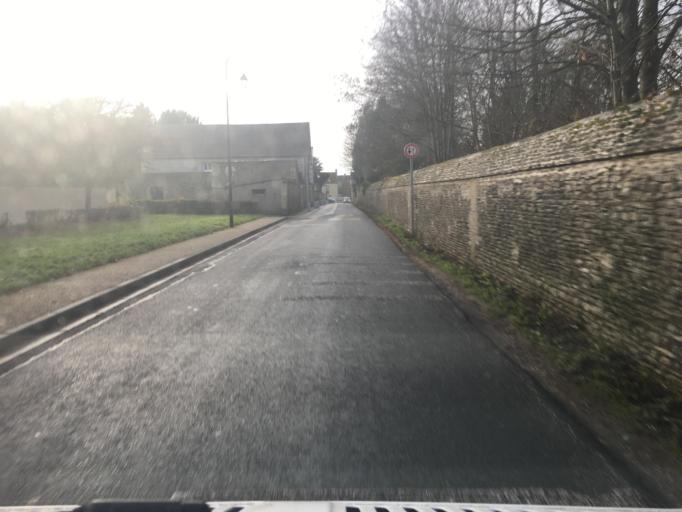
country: FR
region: Lower Normandy
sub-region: Departement du Calvados
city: Rots
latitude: 49.2012
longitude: -0.4771
